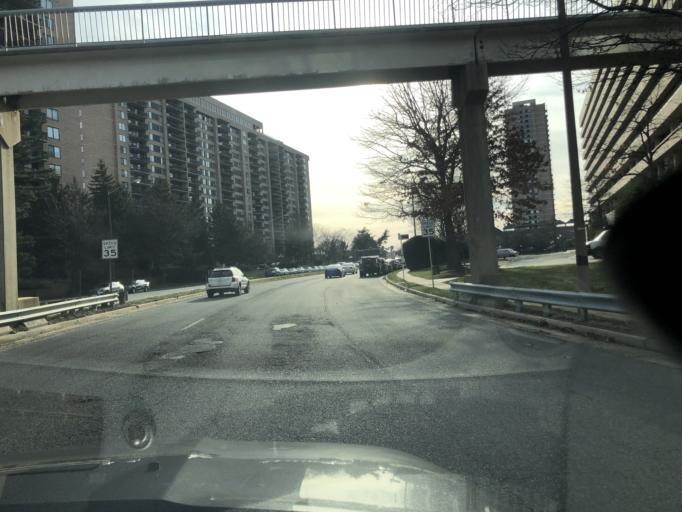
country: US
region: Virginia
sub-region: Fairfax County
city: Baileys Crossroads
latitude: 38.8433
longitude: -77.1161
